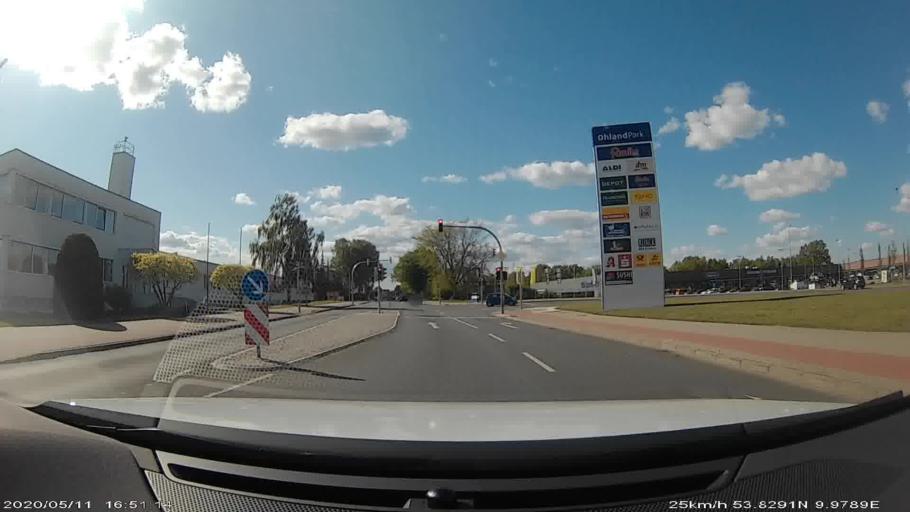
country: DE
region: Schleswig-Holstein
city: Kaltenkirchen
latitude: 53.8336
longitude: 9.9700
